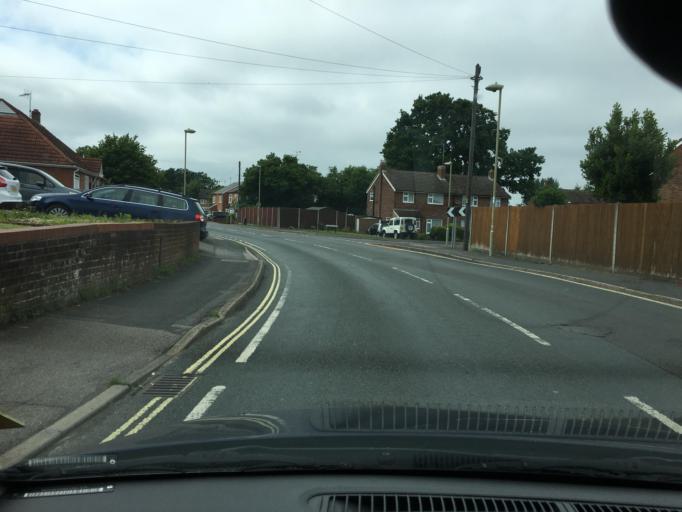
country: GB
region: England
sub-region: Bracknell Forest
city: Sandhurst
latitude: 51.3324
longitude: -0.7814
